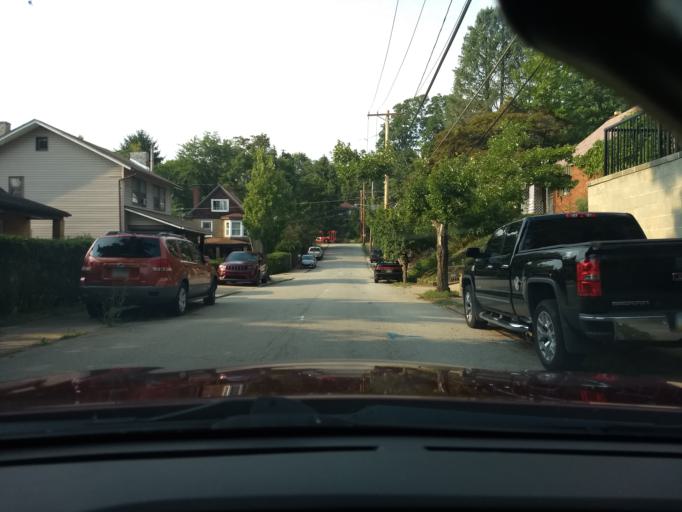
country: US
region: Pennsylvania
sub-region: Allegheny County
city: Wilkinsburg
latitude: 40.4661
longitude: -79.8901
